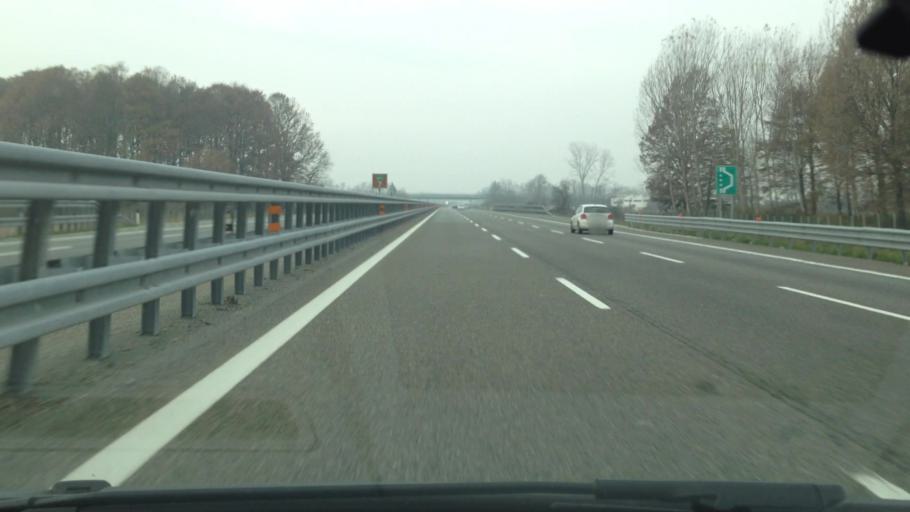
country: IT
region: Piedmont
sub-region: Provincia di Torino
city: Pessione
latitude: 44.9569
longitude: 7.8462
